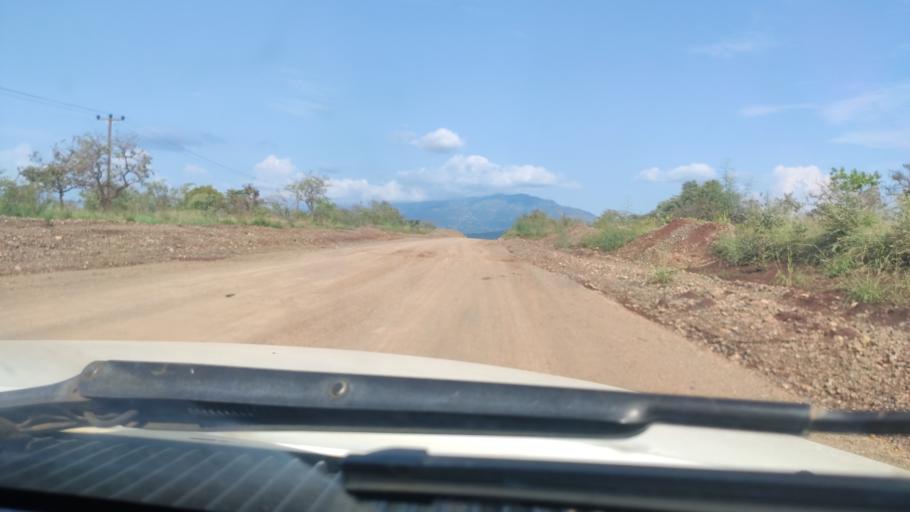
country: ET
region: Southern Nations, Nationalities, and People's Region
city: Felege Neway
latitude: 6.4242
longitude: 37.2443
